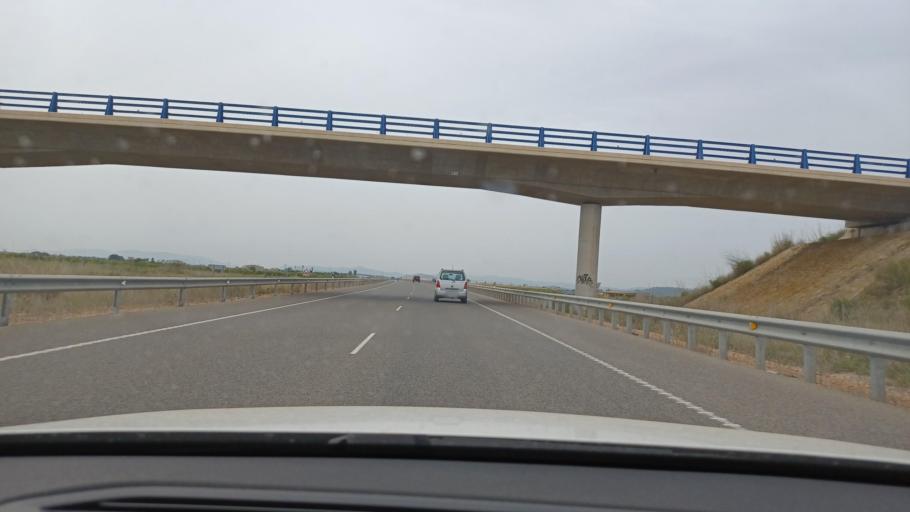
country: ES
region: Catalonia
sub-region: Provincia de Tarragona
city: Alcanar
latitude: 40.5150
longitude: 0.4930
